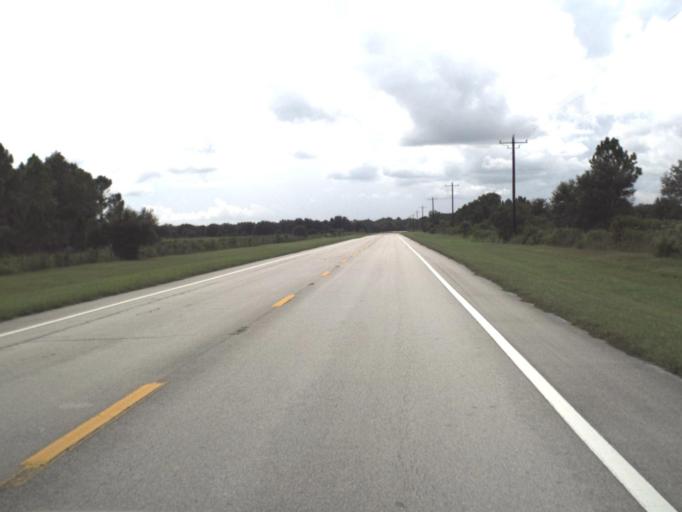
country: US
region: Florida
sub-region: DeSoto County
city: Nocatee
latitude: 27.2042
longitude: -82.0344
